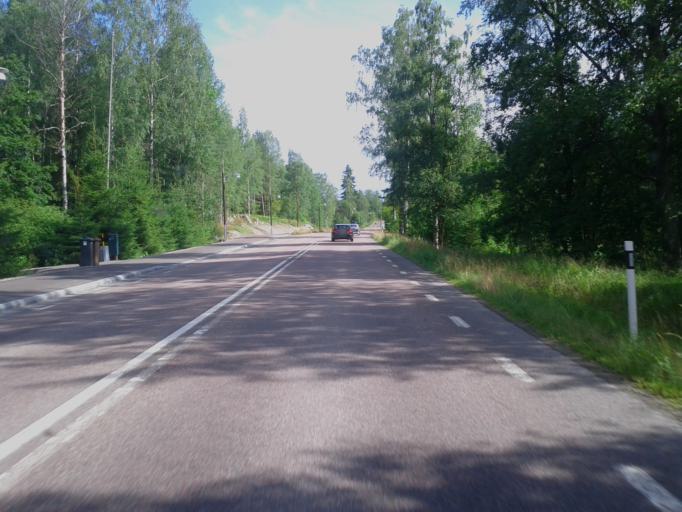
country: SE
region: Dalarna
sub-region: Faluns Kommun
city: Grycksbo
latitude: 60.6676
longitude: 15.5427
